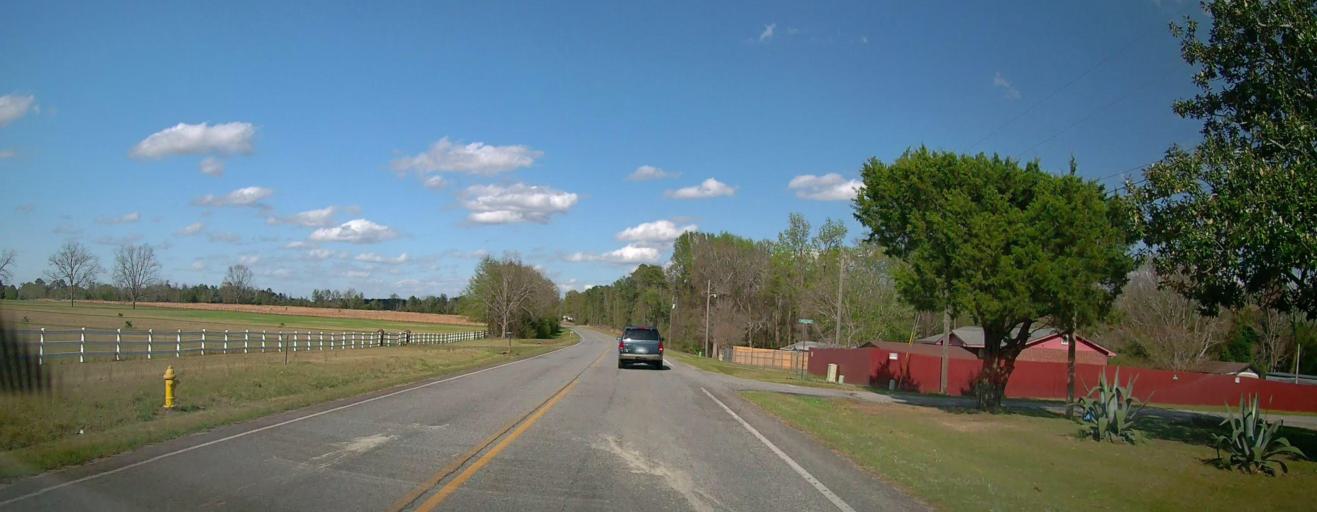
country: US
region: Georgia
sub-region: Baldwin County
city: Hardwick
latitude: 33.0106
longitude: -83.2434
